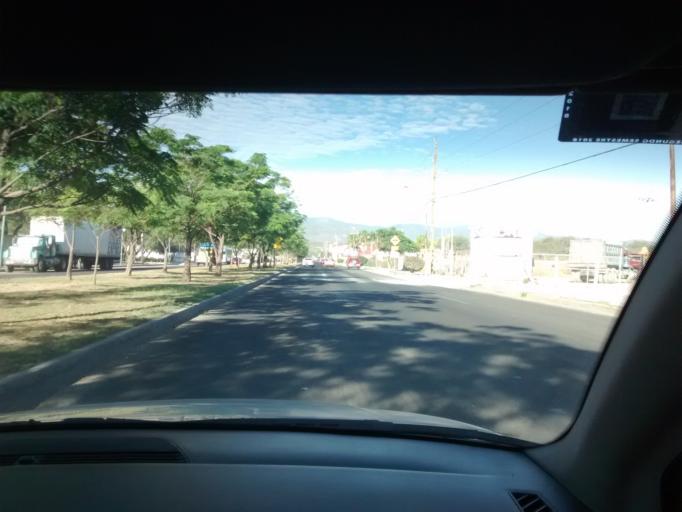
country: MX
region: Puebla
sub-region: Santiago Miahuatlan
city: San Jose Monte Chiquito
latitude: 18.4801
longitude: -97.4196
